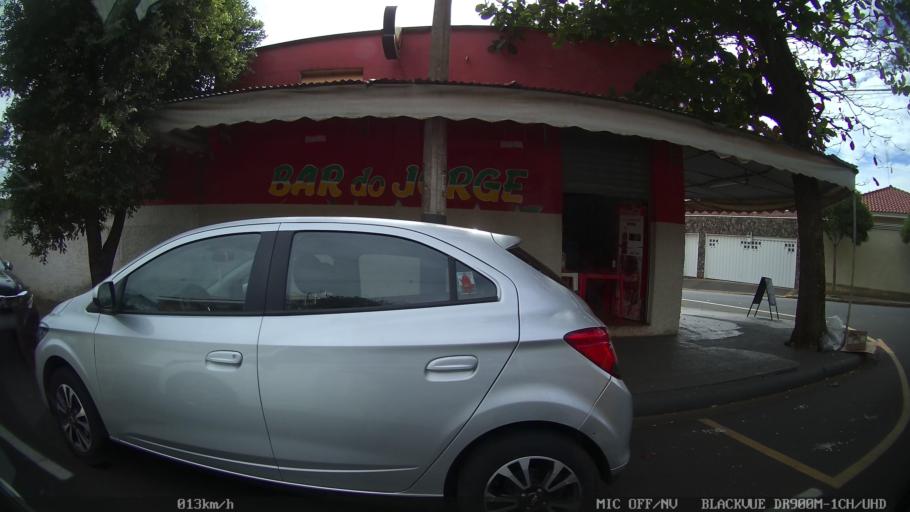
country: BR
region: Sao Paulo
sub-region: Catanduva
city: Catanduva
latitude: -21.1455
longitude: -48.9679
